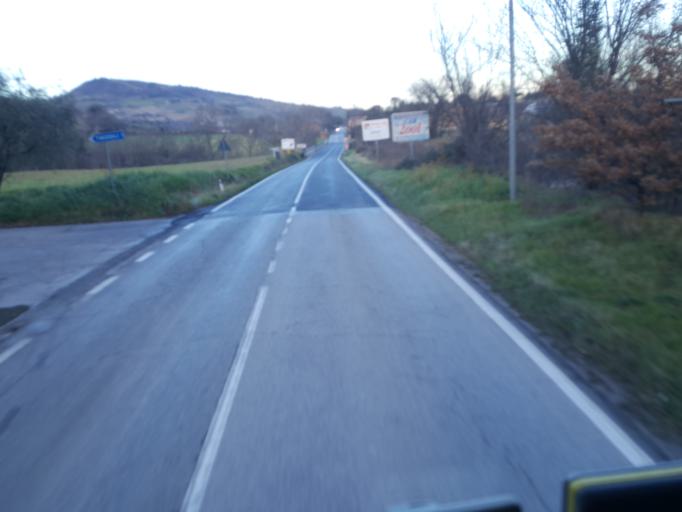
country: IT
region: The Marches
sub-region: Provincia di Macerata
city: San Severino Marche
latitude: 43.2427
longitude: 13.2219
